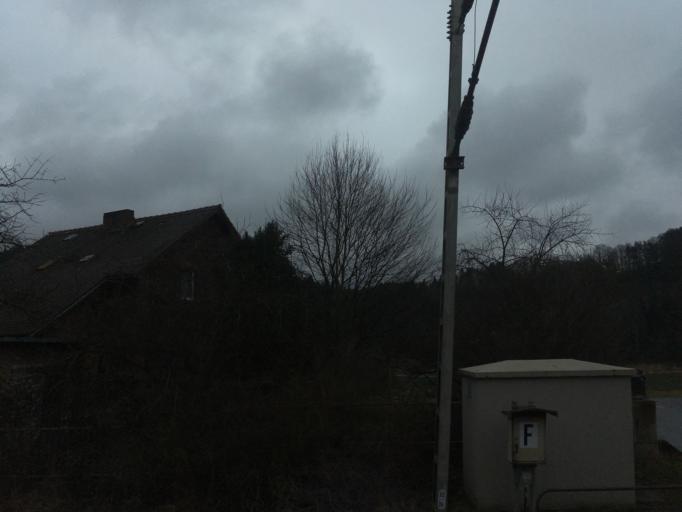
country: DE
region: Saxony
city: Konigstein
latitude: 50.9481
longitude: 14.0823
